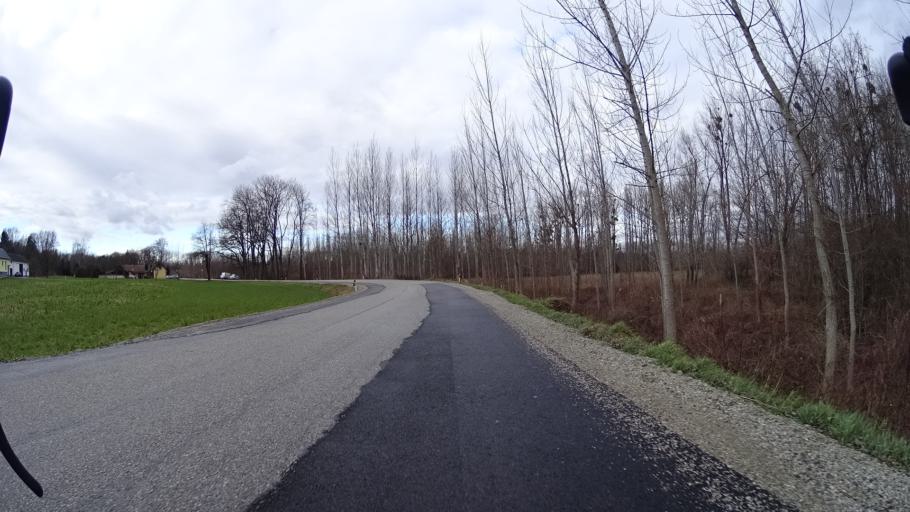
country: AT
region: Lower Austria
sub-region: Politischer Bezirk Tulln
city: Langenrohr
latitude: 48.3304
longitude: 15.9962
